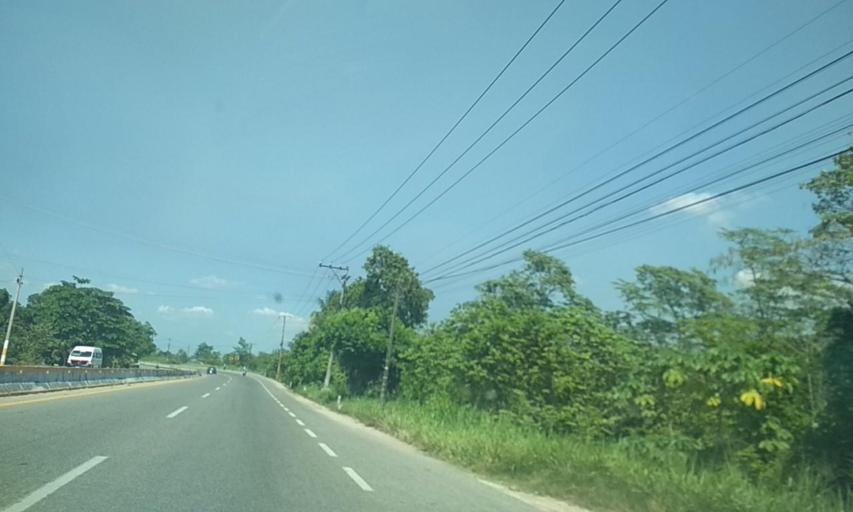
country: MX
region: Tabasco
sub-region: Huimanguillo
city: El Dorado
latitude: 17.8622
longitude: -93.3872
